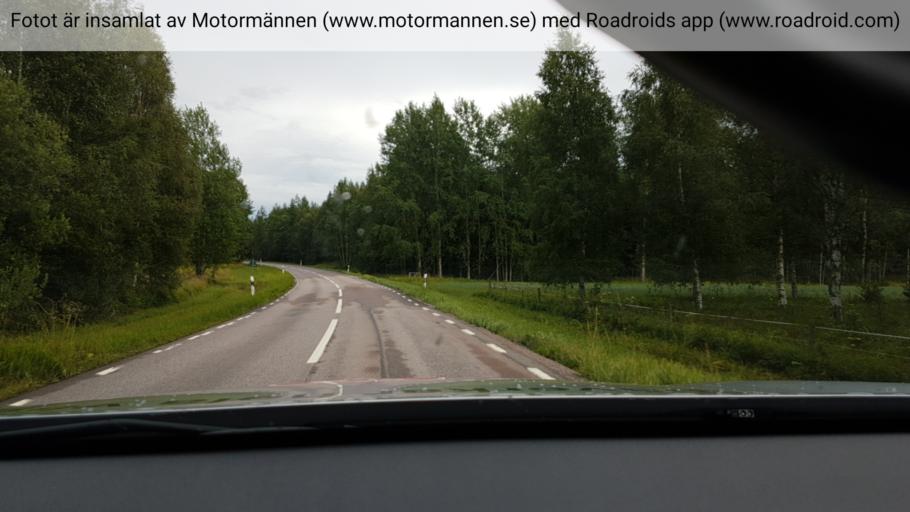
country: SE
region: Uppsala
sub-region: Osthammars Kommun
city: Osterbybruk
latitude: 60.3644
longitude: 18.0357
